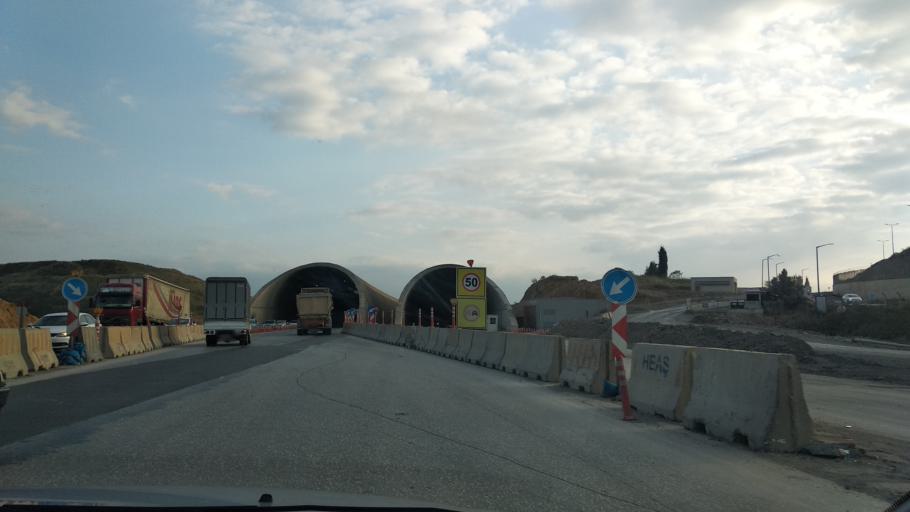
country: TR
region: Istanbul
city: Icmeler
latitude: 40.9047
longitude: 29.3277
